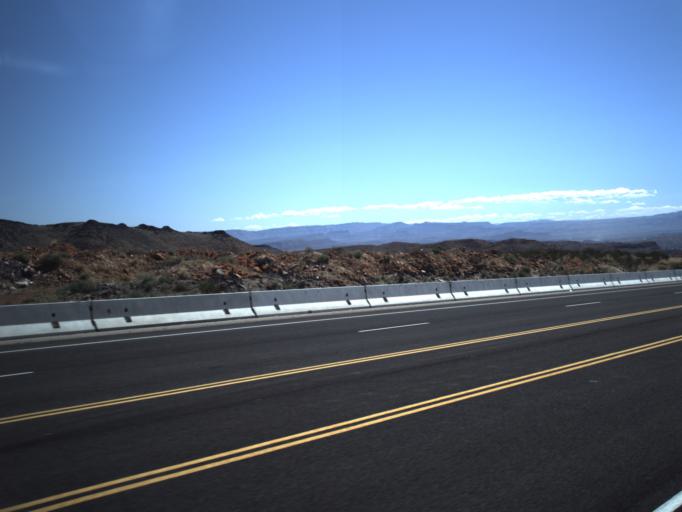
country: US
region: Utah
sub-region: Washington County
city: Santa Clara
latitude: 37.1734
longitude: -113.6188
